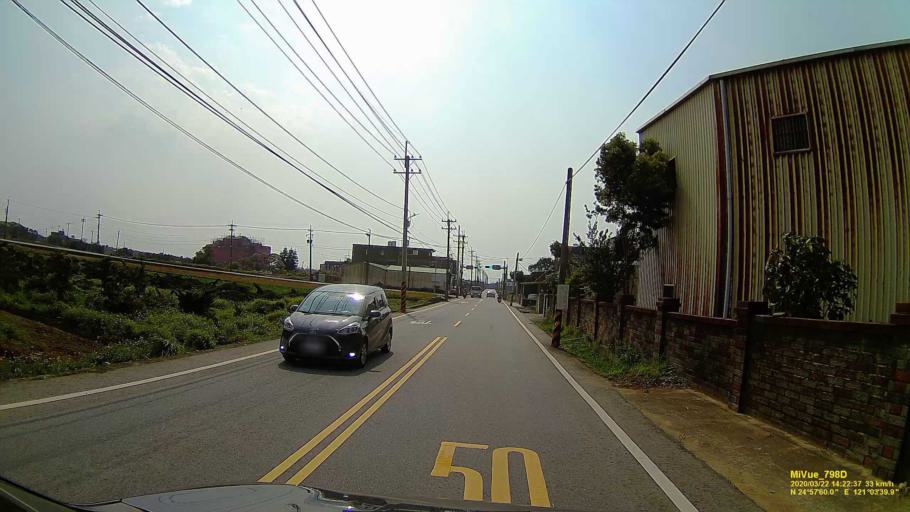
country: TW
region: Taiwan
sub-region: Hsinchu
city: Zhubei
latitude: 24.9666
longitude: 121.0609
